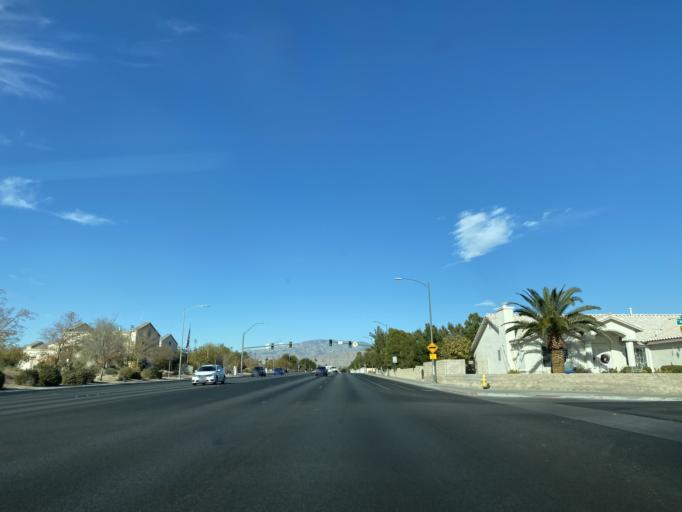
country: US
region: Nevada
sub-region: Clark County
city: Las Vegas
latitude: 36.2857
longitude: -115.2604
